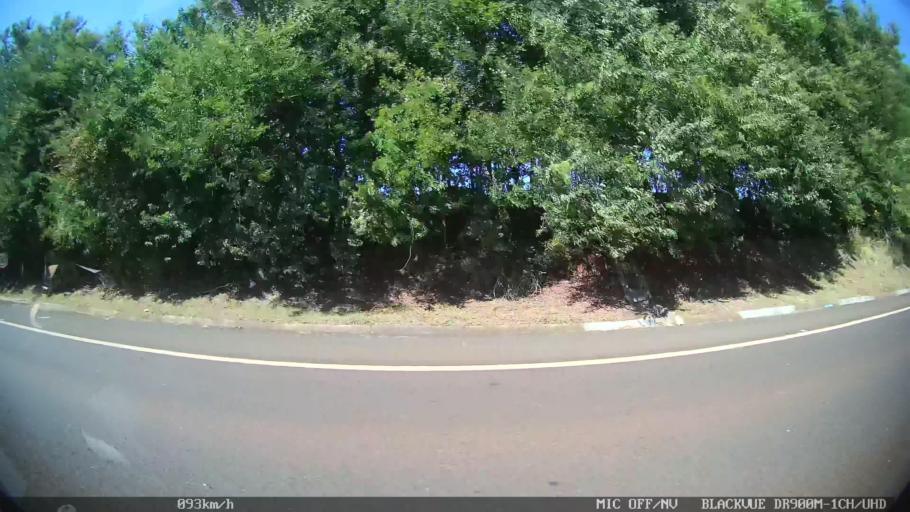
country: BR
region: Sao Paulo
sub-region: Franca
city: Franca
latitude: -20.5837
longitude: -47.4307
